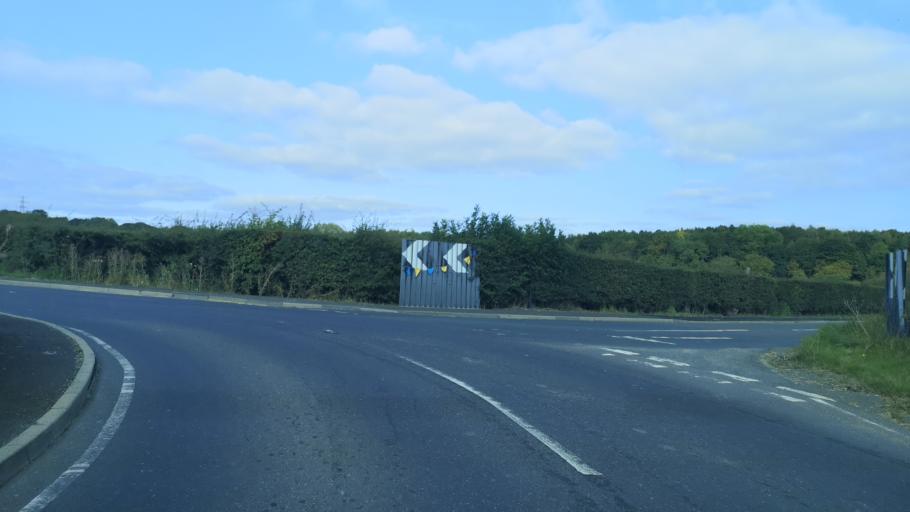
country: GB
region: England
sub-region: City and Borough of Wakefield
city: Walton
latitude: 53.6282
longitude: -1.4630
